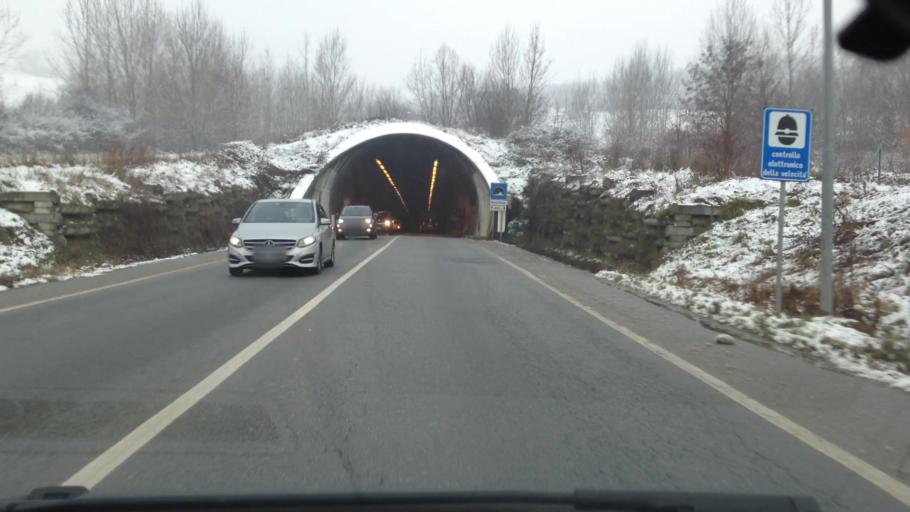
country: IT
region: Piedmont
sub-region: Provincia di Asti
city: Piano-Molini d'Isola
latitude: 44.8317
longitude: 8.2019
